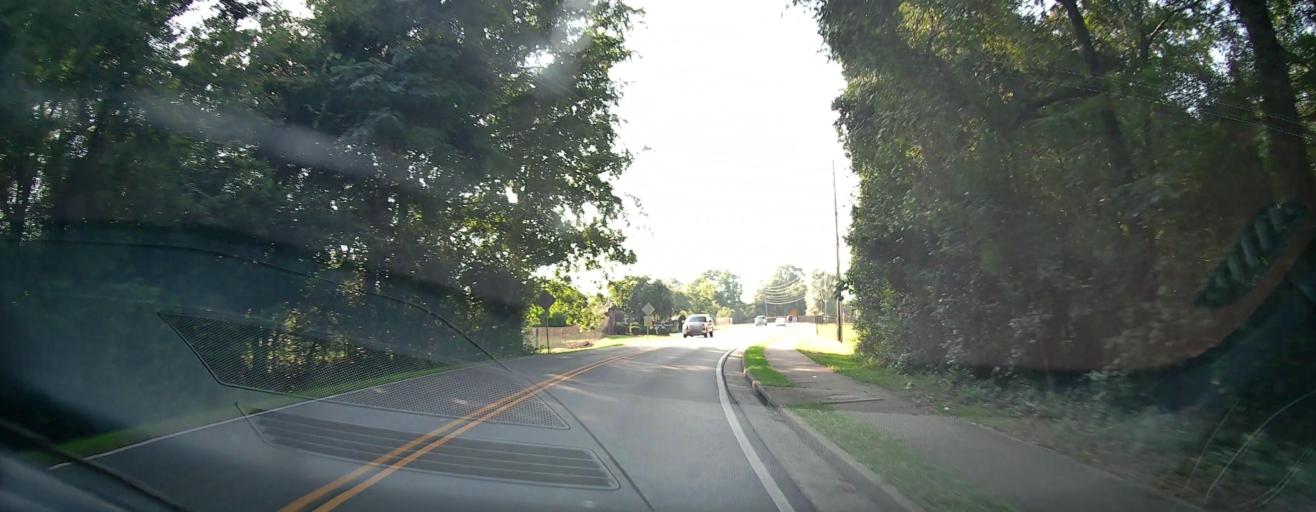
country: US
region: Georgia
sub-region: Houston County
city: Perry
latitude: 32.4685
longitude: -83.7344
